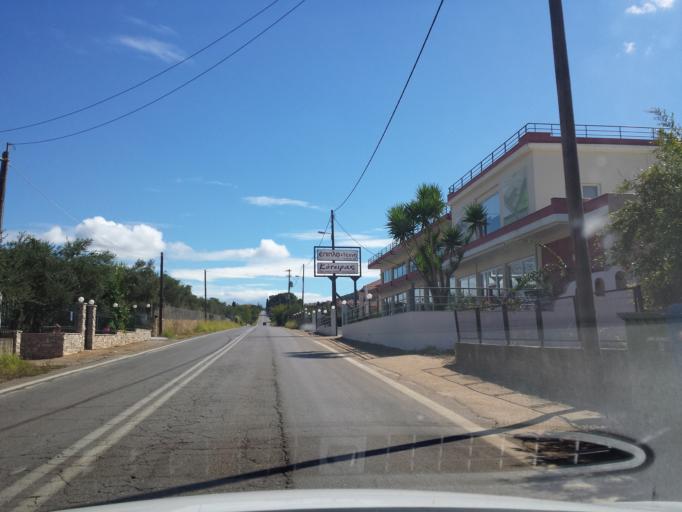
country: GR
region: Peloponnese
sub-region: Nomos Messinias
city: Vlakhopoulon
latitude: 36.9587
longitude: 21.7763
